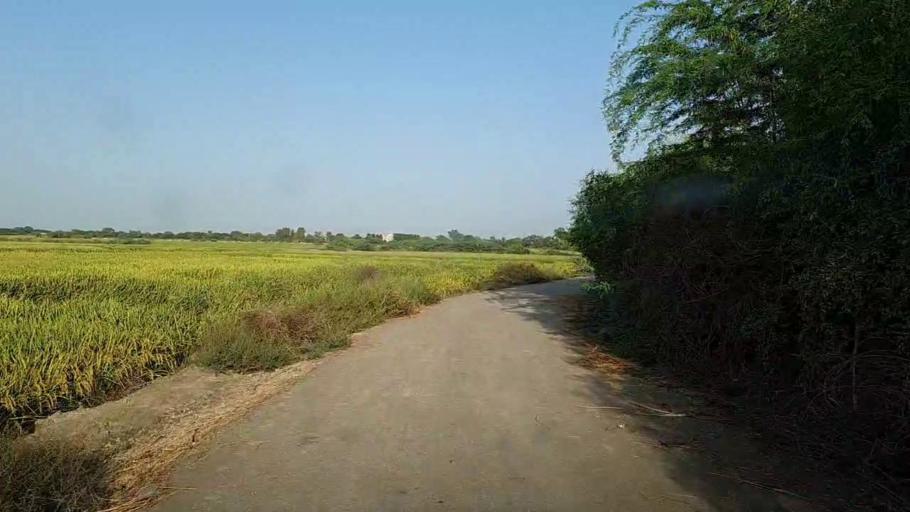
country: PK
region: Sindh
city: Bulri
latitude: 24.7566
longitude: 68.4071
